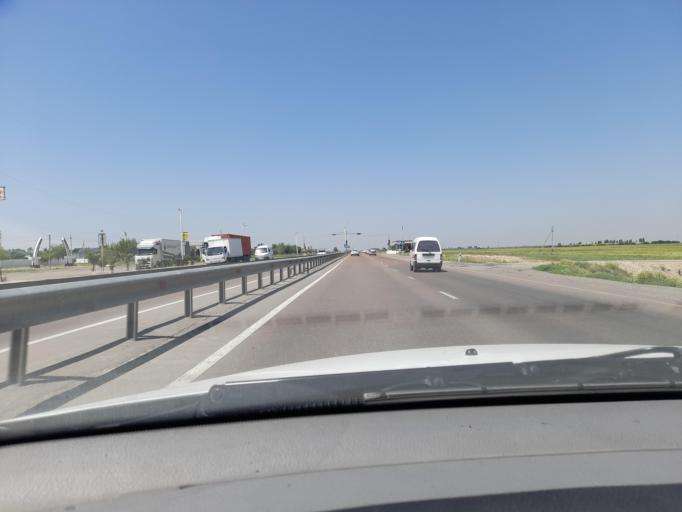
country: KZ
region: Ongtustik Qazaqstan
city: Myrzakent
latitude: 40.5058
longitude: 68.5137
